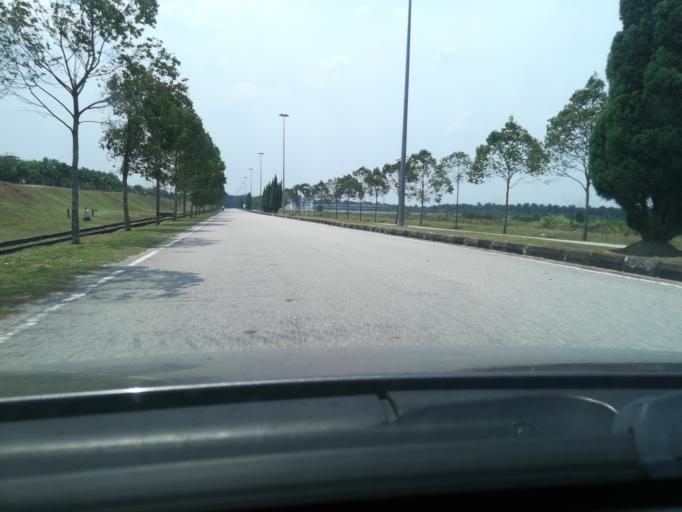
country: MY
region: Kedah
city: Kulim
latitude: 5.4254
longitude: 100.5774
